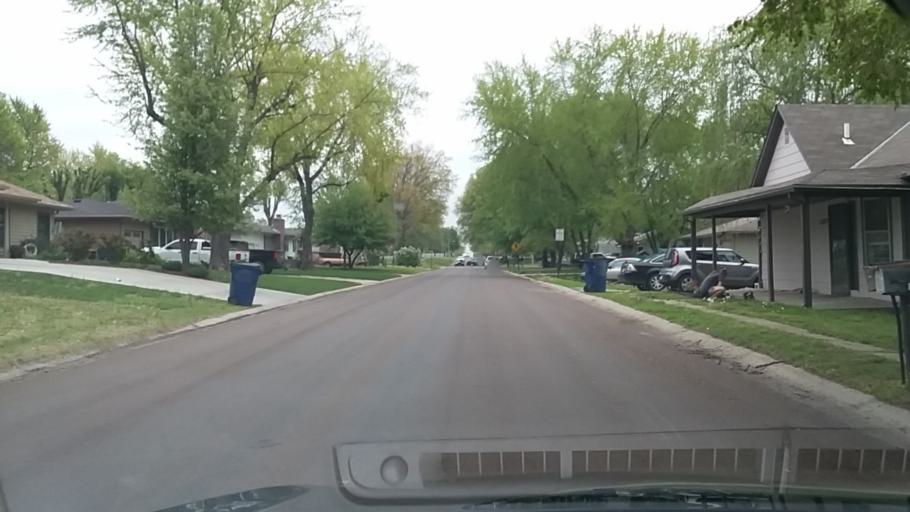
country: US
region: Kansas
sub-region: Douglas County
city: Eudora
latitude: 38.9371
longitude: -95.0979
